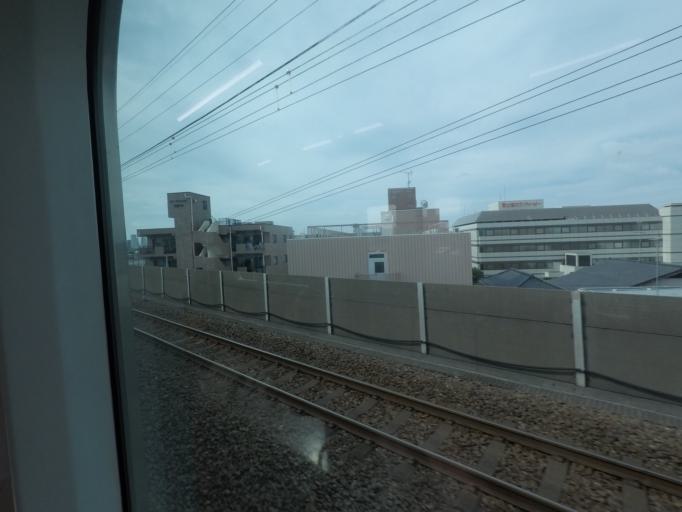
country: JP
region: Kanagawa
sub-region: Kawasaki-shi
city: Kawasaki
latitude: 35.5794
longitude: 139.6445
